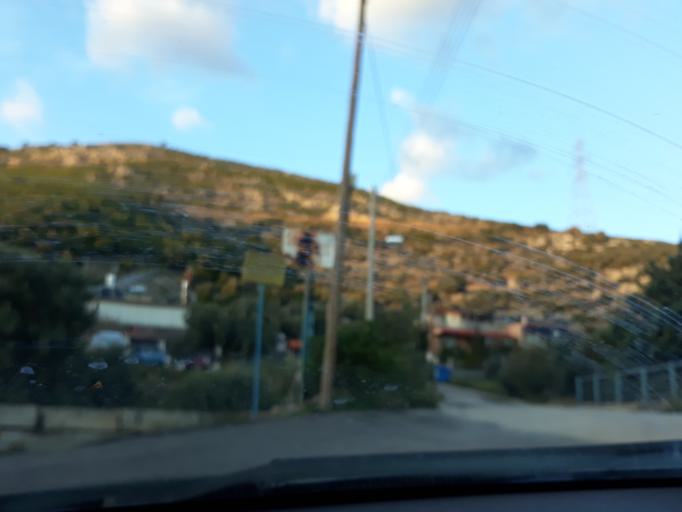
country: GR
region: Attica
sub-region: Nomarchia Dytikis Attikis
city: Ano Liosia
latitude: 38.0983
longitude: 23.6998
